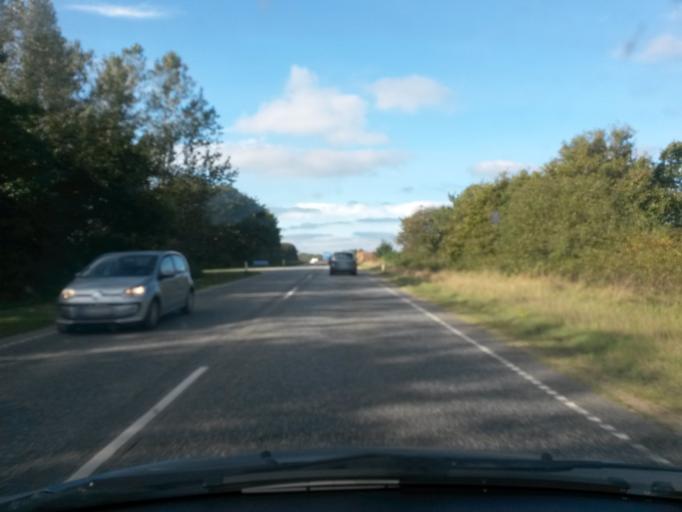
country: DK
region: Central Jutland
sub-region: Herning Kommune
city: Avlum
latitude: 56.2748
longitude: 8.7609
